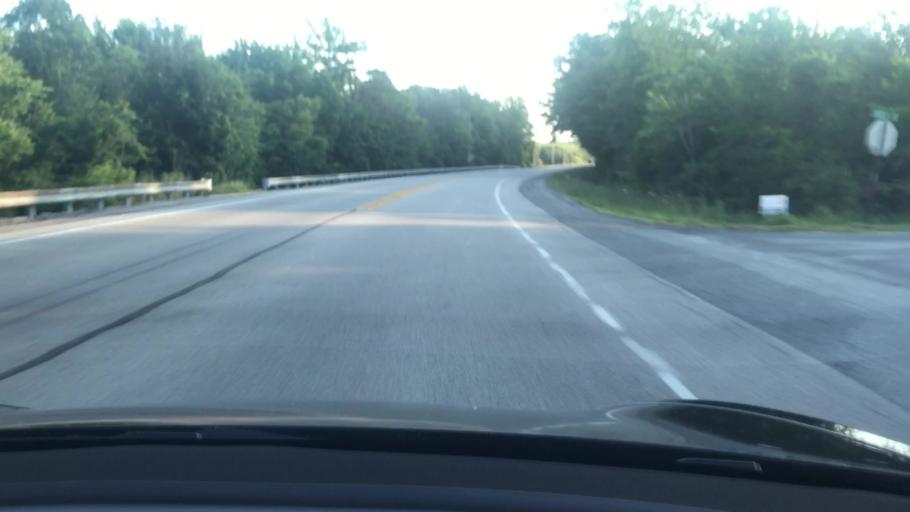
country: US
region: Pennsylvania
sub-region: York County
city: Valley Green
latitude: 40.1050
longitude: -76.8649
